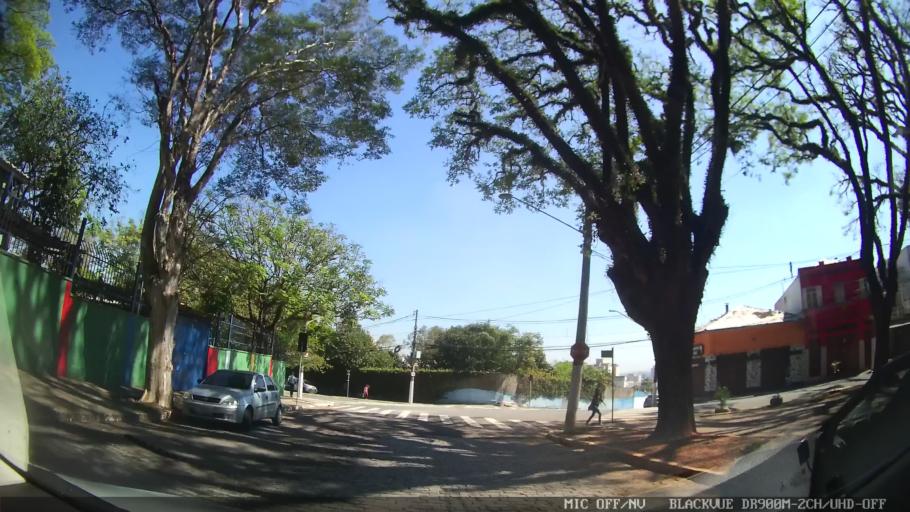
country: BR
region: Sao Paulo
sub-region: Sao Paulo
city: Sao Paulo
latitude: -23.5099
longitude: -46.6574
